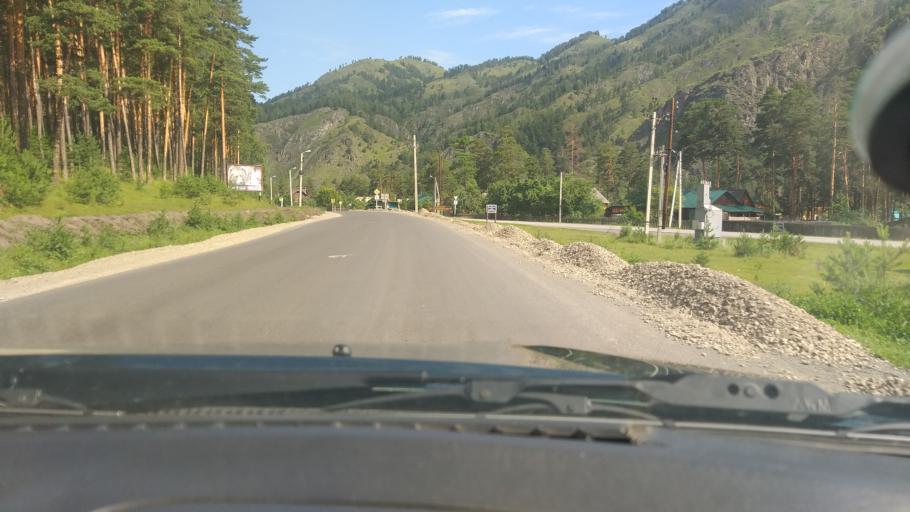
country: RU
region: Altay
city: Chemal
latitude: 51.3976
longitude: 86.0231
